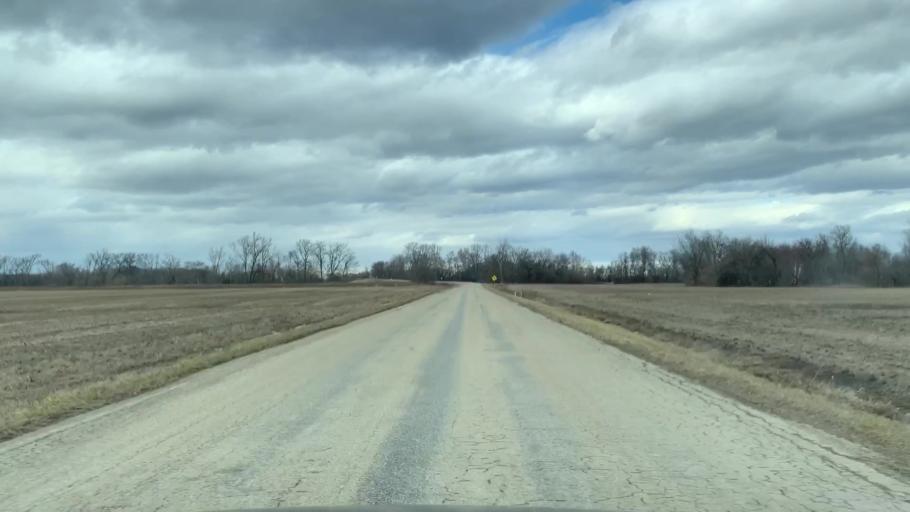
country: US
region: Kansas
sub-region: Allen County
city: Humboldt
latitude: 37.7993
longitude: -95.4706
